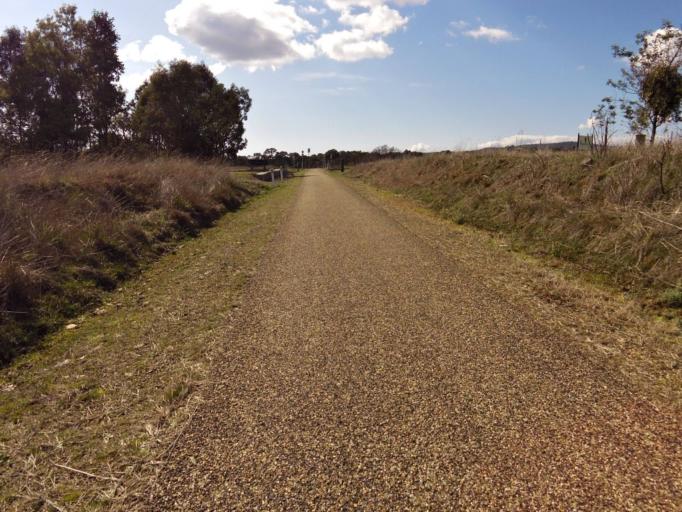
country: AU
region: Victoria
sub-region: Wangaratta
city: Wangaratta
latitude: -36.3952
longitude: 146.6569
